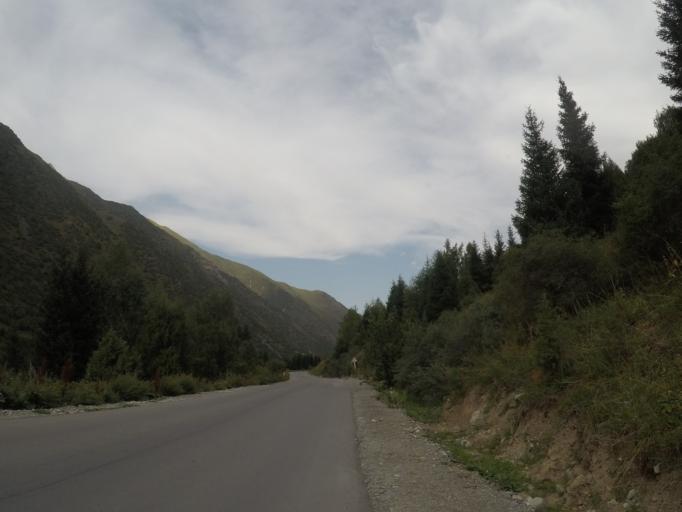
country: KG
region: Chuy
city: Bishkek
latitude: 42.5892
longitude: 74.4838
